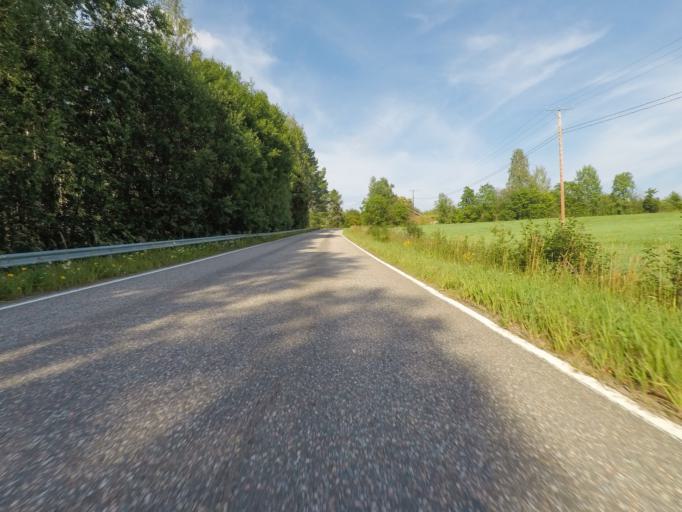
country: FI
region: Southern Savonia
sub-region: Savonlinna
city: Sulkava
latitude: 61.7608
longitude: 28.2323
